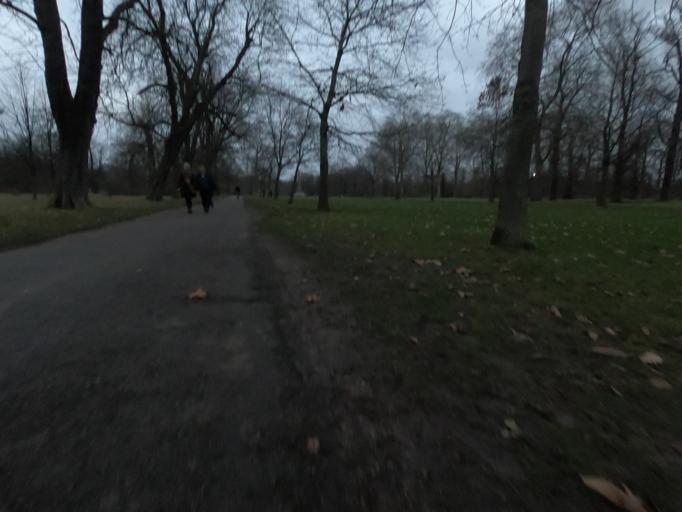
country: GB
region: England
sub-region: Greater London
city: Bayswater
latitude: 51.5082
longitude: -0.1807
